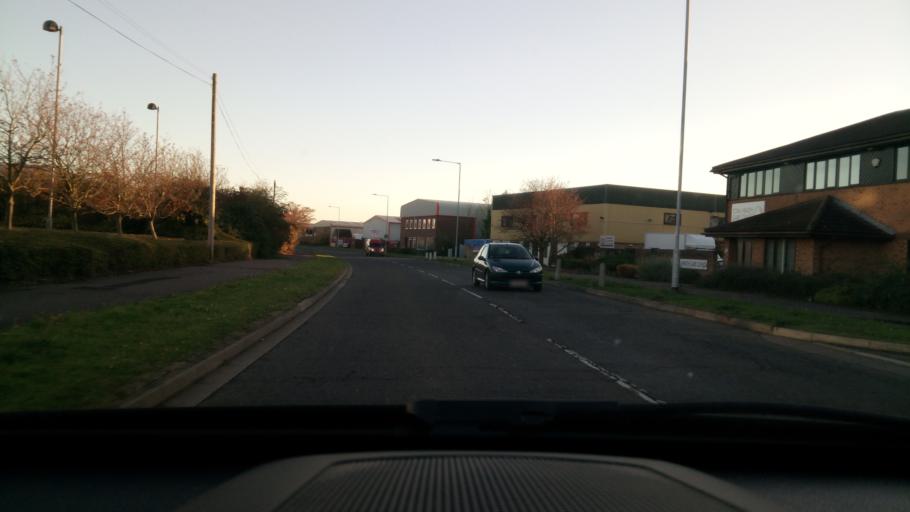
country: GB
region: England
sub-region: Peterborough
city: Marholm
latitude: 52.6174
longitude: -0.2903
